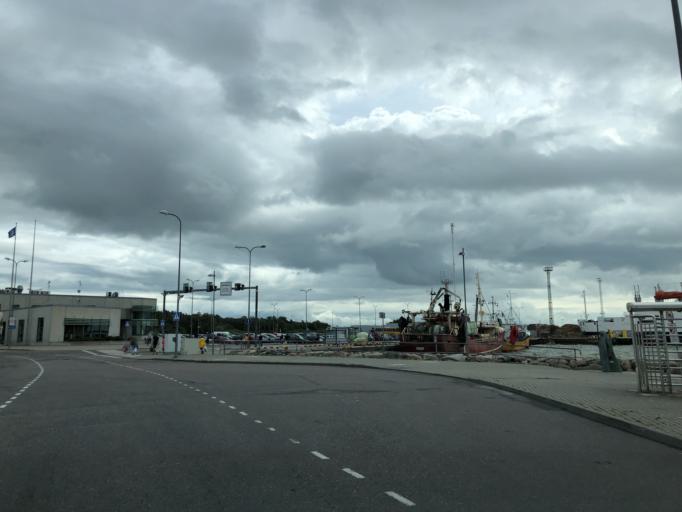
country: EE
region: Laeaene
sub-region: Haapsalu linn
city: Haapsalu
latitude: 58.9064
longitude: 23.4230
